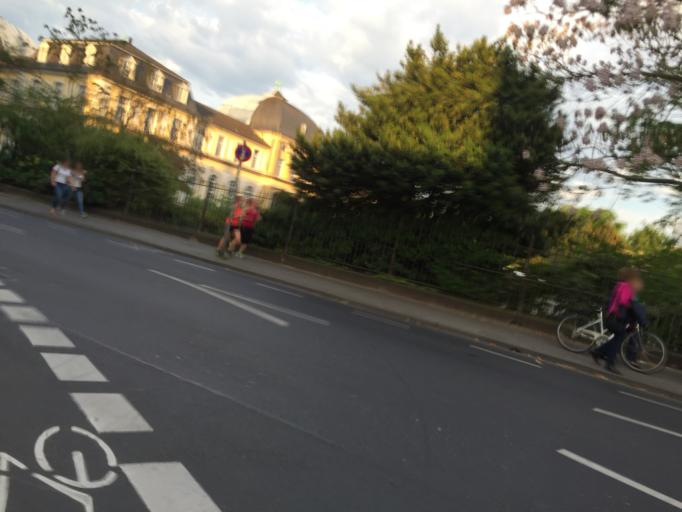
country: DE
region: North Rhine-Westphalia
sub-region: Regierungsbezirk Koln
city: Bonn
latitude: 50.7249
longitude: 7.0906
